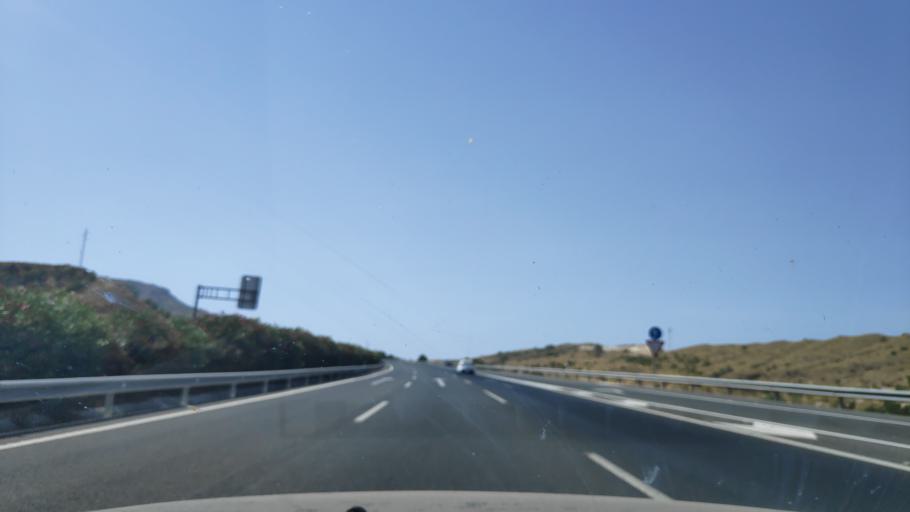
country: ES
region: Murcia
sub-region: Murcia
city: Ulea
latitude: 38.1615
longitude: -1.3003
